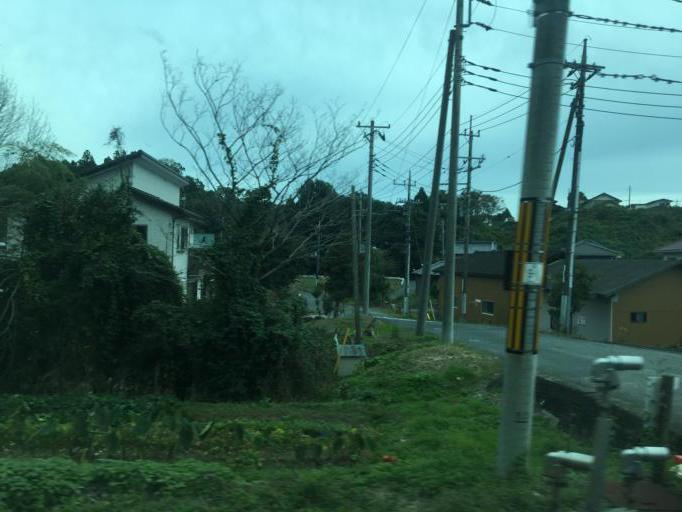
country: JP
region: Ibaraki
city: Kitaibaraki
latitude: 36.8550
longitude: 140.7793
